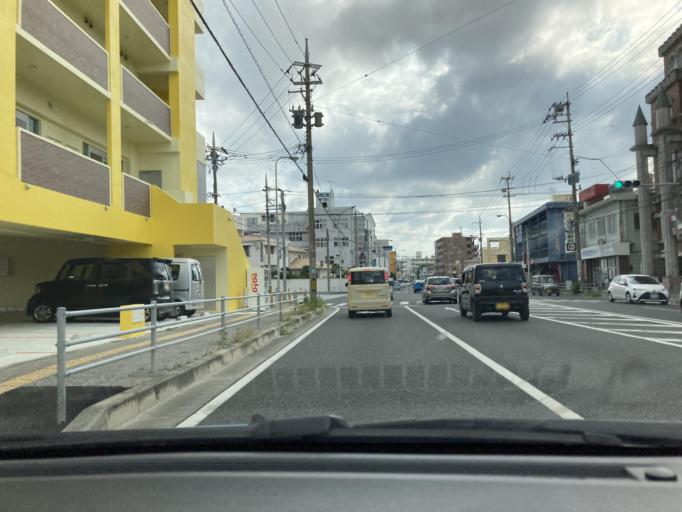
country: JP
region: Okinawa
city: Ginowan
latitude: 26.2084
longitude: 127.7579
